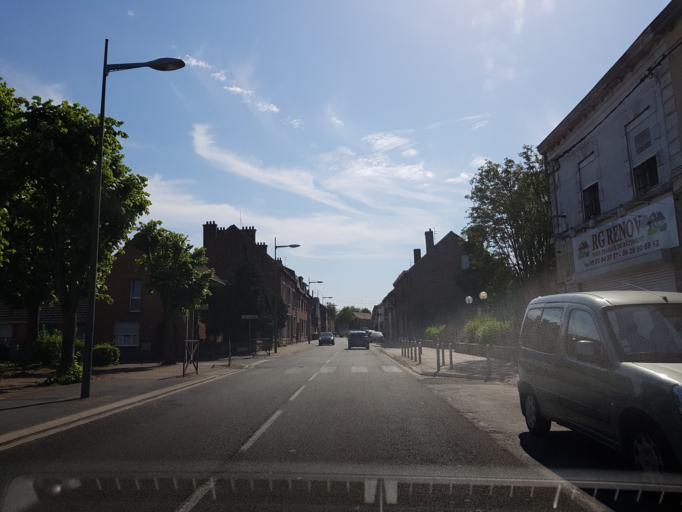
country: FR
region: Nord-Pas-de-Calais
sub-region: Departement du Nord
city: Lourches
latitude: 50.3141
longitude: 3.3511
